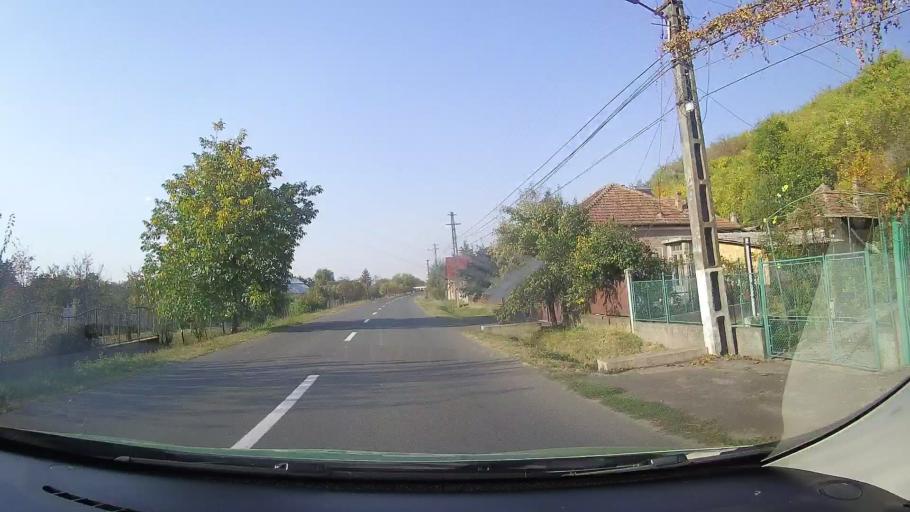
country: RO
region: Arad
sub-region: Comuna Paulis
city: Paulis
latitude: 46.1133
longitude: 21.5969
